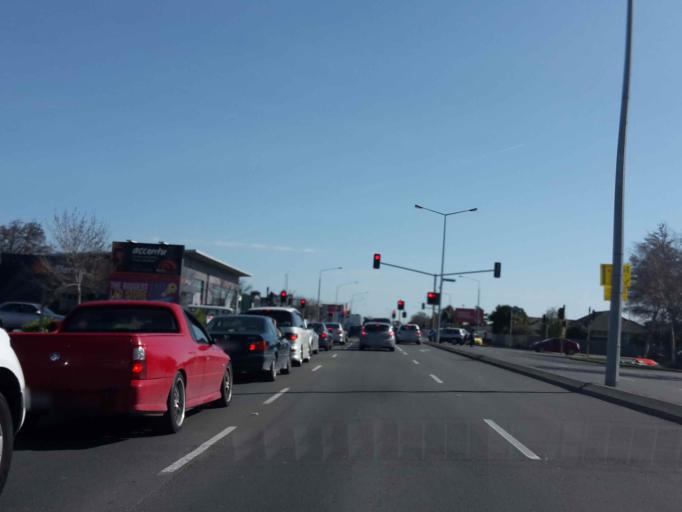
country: NZ
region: Canterbury
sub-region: Christchurch City
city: Christchurch
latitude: -43.5382
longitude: 172.5883
